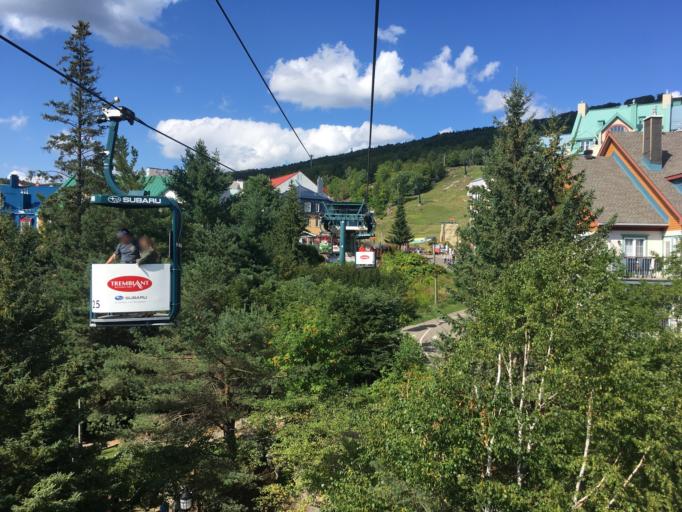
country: CA
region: Quebec
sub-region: Laurentides
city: Mont-Tremblant
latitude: 46.2119
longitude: -74.5849
